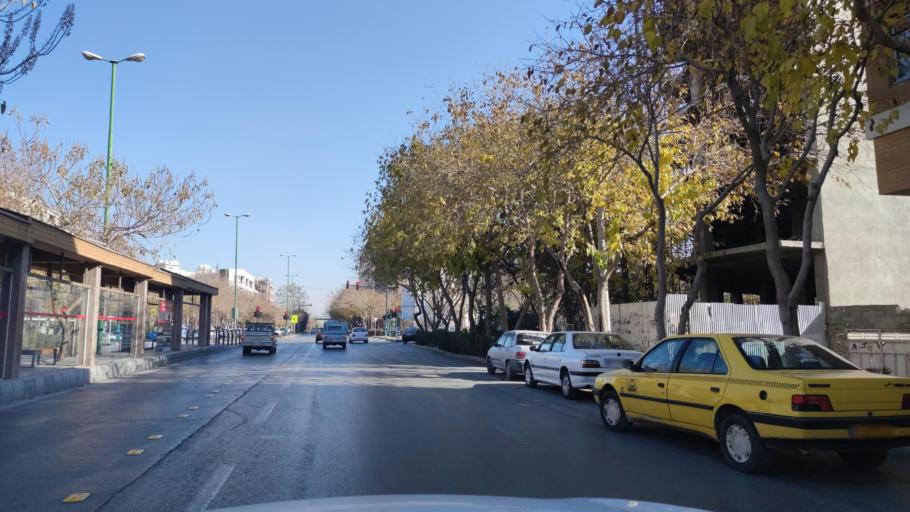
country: IR
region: Isfahan
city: Isfahan
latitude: 32.6800
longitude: 51.6571
